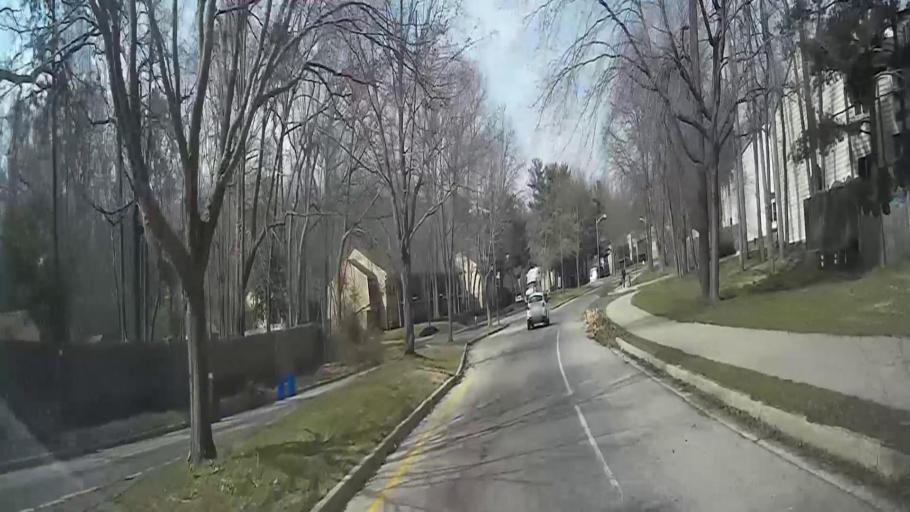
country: US
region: New Jersey
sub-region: Burlington County
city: Marlton
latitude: 39.8741
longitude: -74.8660
